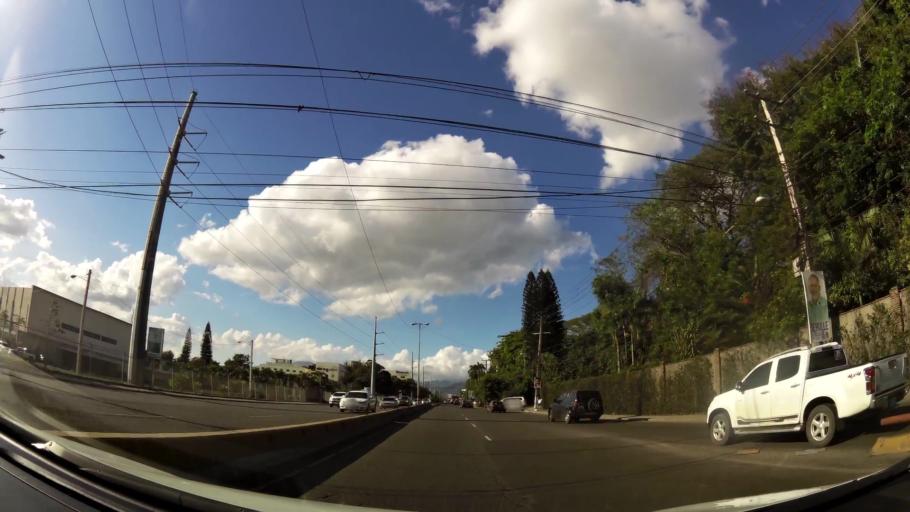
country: DO
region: Santiago
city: Santiago de los Caballeros
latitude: 19.4628
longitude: -70.6864
